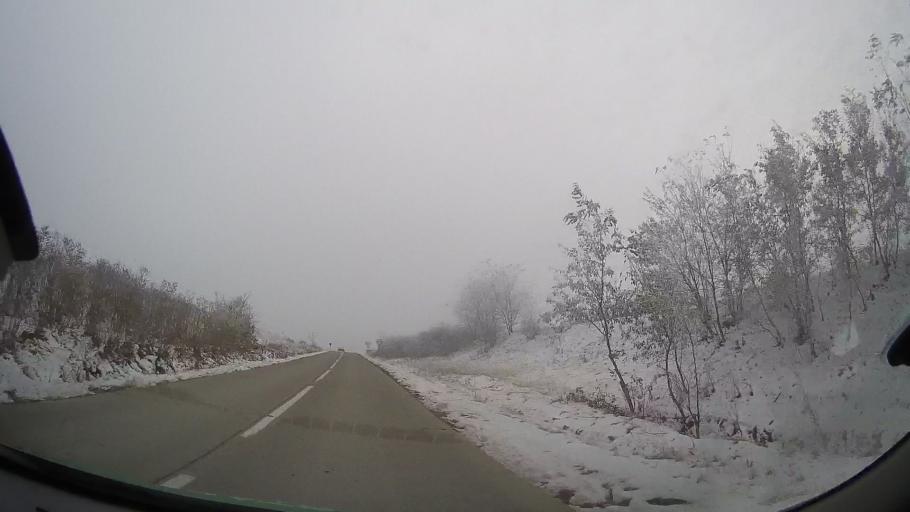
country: RO
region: Vaslui
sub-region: Comuna Ivesti
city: Ivesti
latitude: 46.2060
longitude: 27.5062
